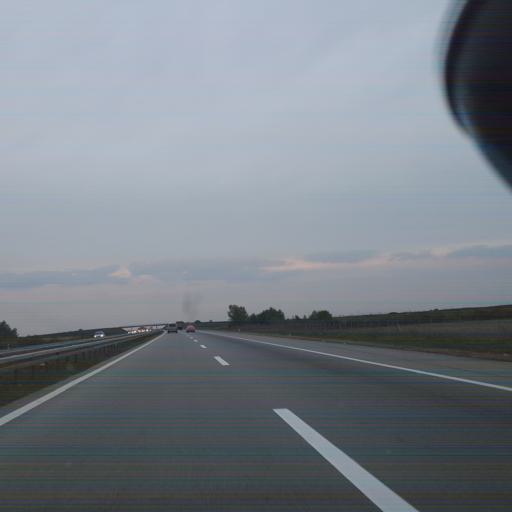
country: RS
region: Autonomna Pokrajina Vojvodina
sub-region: Juznobacki Okrug
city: Kovilj
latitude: 45.2007
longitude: 20.0727
